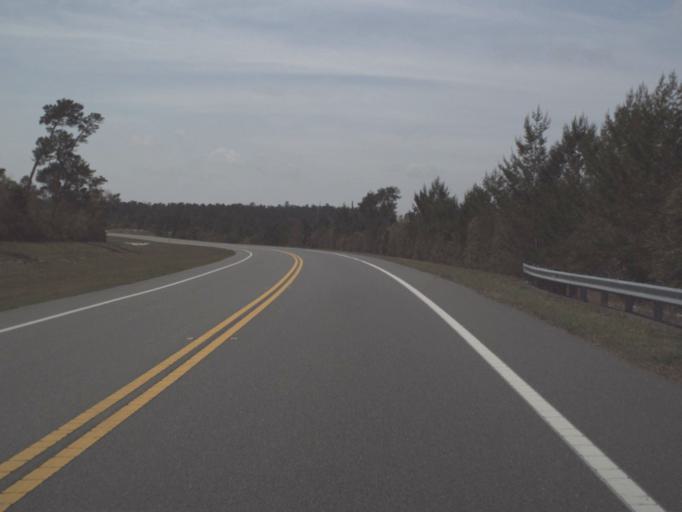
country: US
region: Florida
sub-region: Lake County
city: Astor
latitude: 29.2111
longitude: -81.6585
